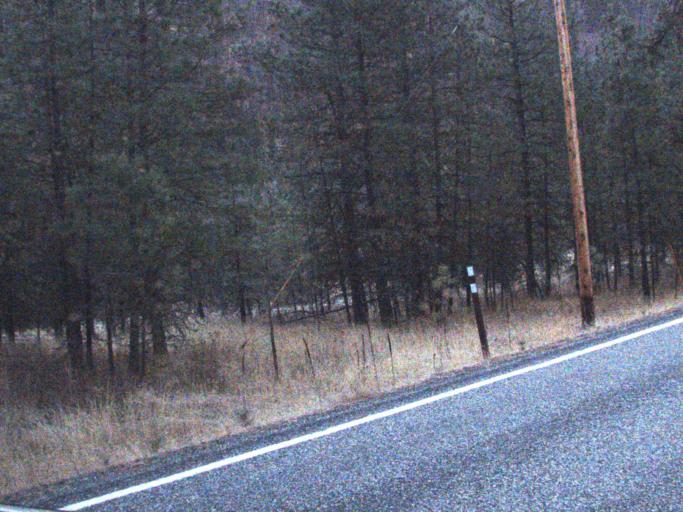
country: US
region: Washington
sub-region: Ferry County
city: Republic
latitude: 48.4031
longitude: -118.7323
